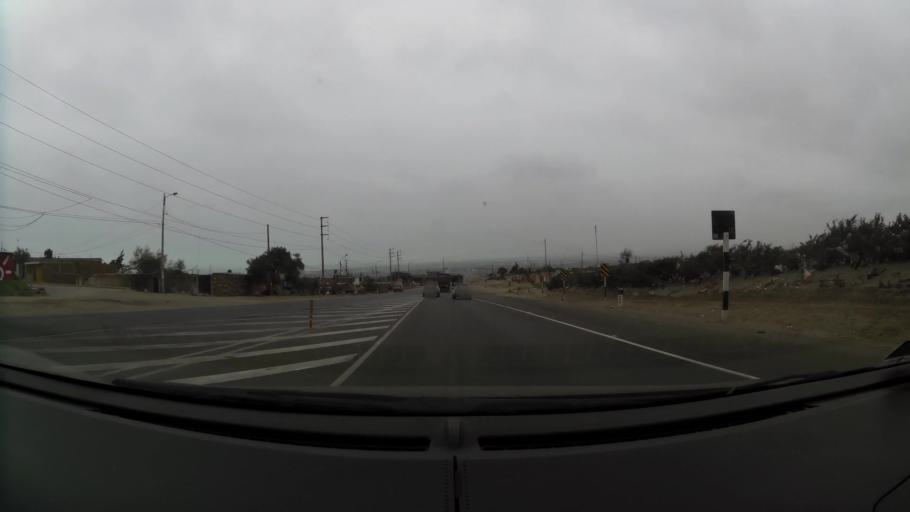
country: PE
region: La Libertad
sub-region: Provincia de Trujillo
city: Moche
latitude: -8.1860
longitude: -78.9824
